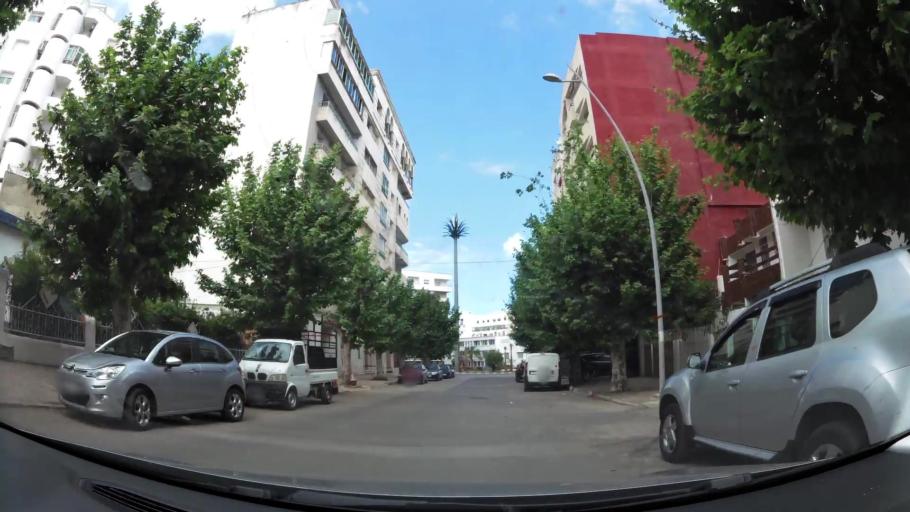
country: MA
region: Gharb-Chrarda-Beni Hssen
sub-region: Kenitra Province
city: Kenitra
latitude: 34.2555
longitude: -6.5860
